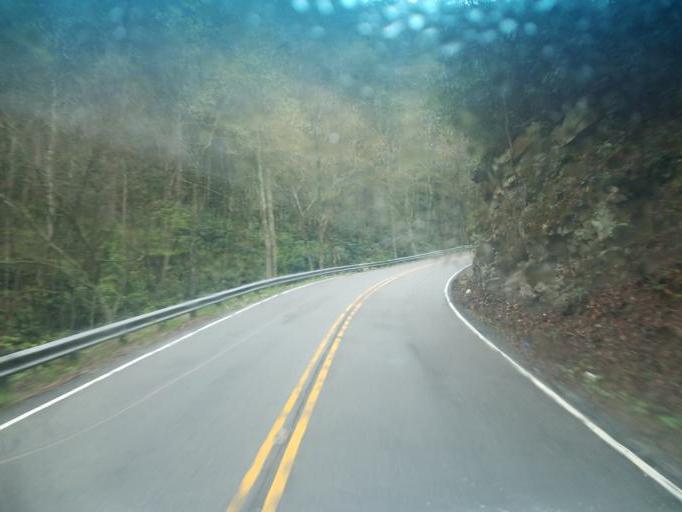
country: US
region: Virginia
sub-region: Washington County
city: Glade Spring
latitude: 36.6446
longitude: -81.7159
